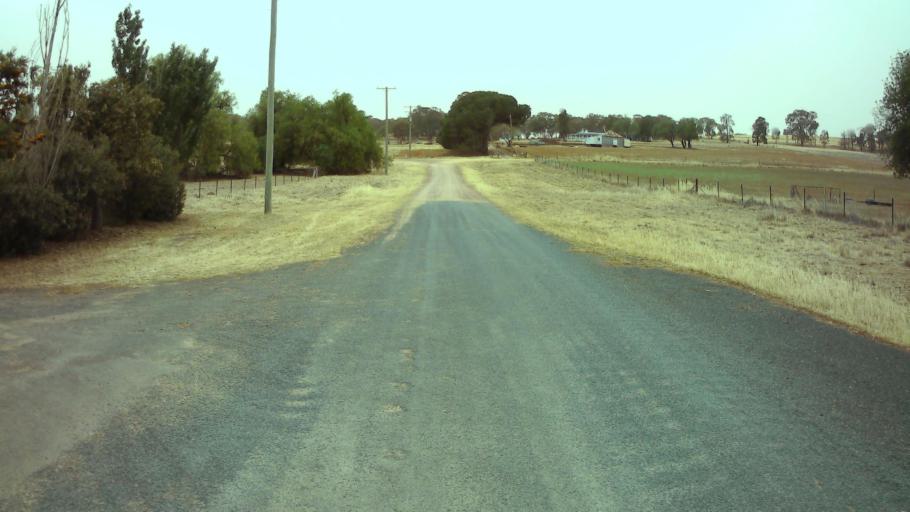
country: AU
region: New South Wales
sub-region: Weddin
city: Grenfell
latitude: -33.9074
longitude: 148.1713
